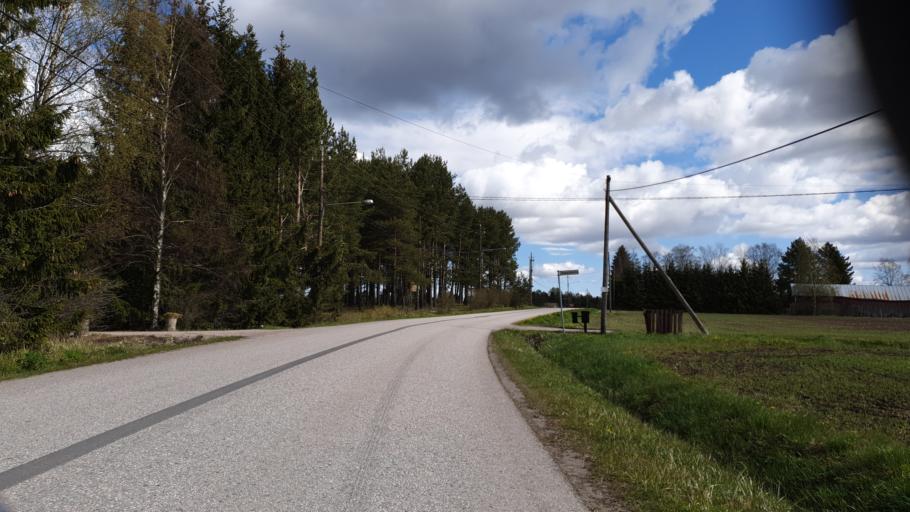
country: FI
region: Uusimaa
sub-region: Helsinki
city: Tuusula
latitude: 60.3956
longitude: 24.9185
